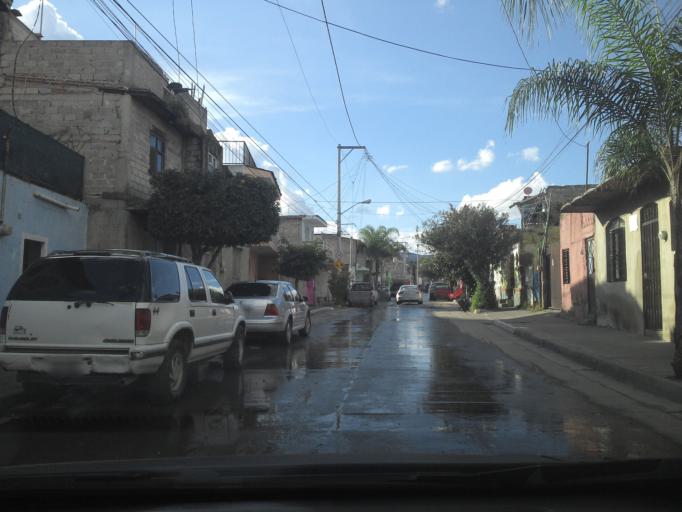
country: MX
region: Jalisco
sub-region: Tlajomulco de Zuniga
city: Palomar
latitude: 20.6192
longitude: -103.4535
